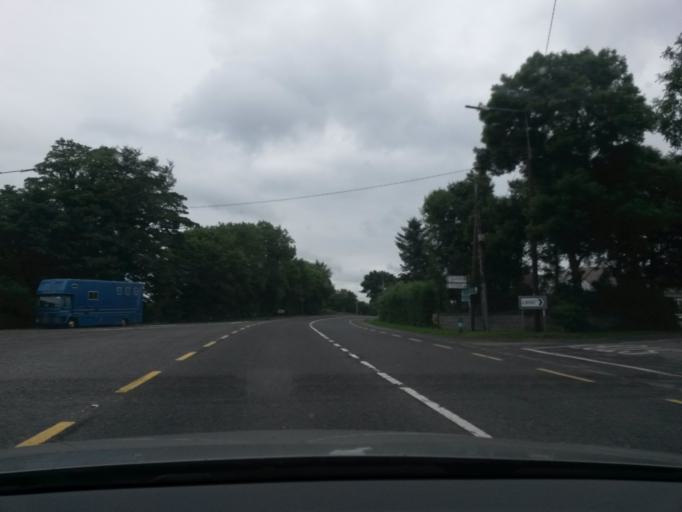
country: IE
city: Ballisodare
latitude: 54.2082
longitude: -8.5336
